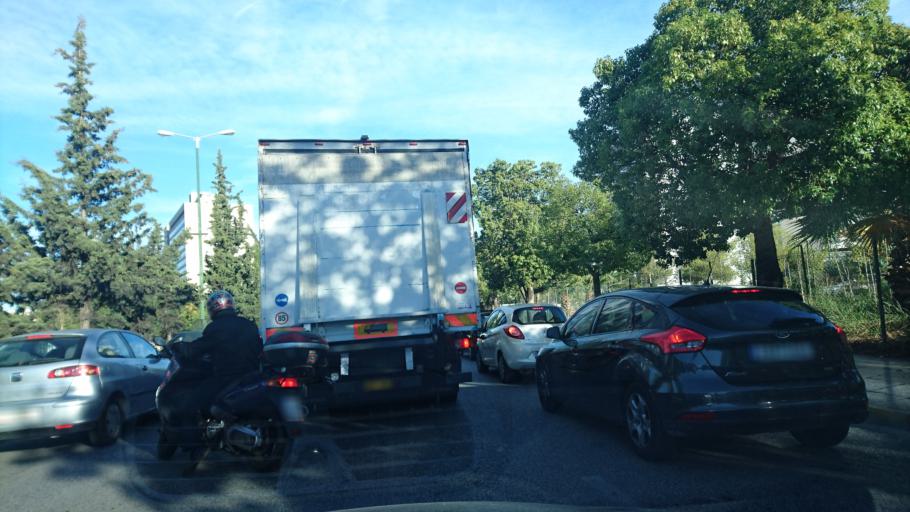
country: GR
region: Attica
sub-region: Nomarchia Athinas
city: Papagou
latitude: 37.9880
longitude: 23.7796
